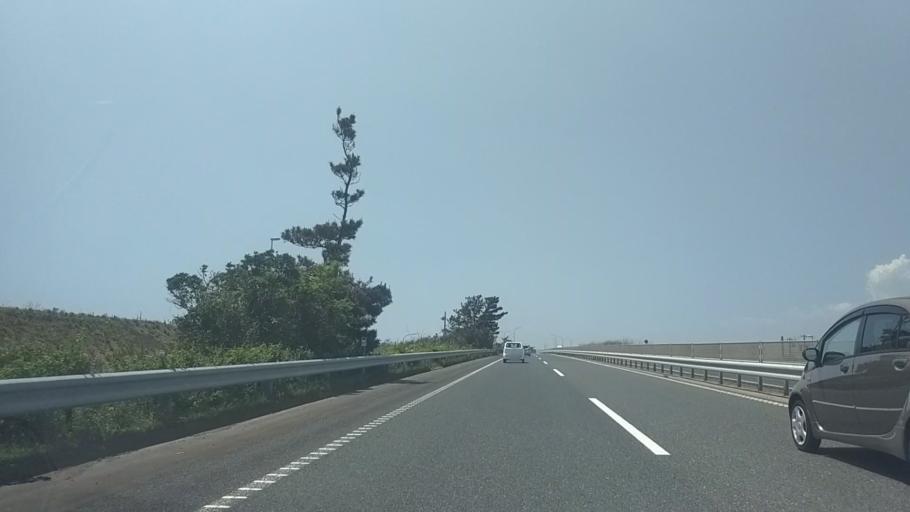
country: JP
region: Shizuoka
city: Hamamatsu
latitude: 34.6757
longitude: 137.6500
